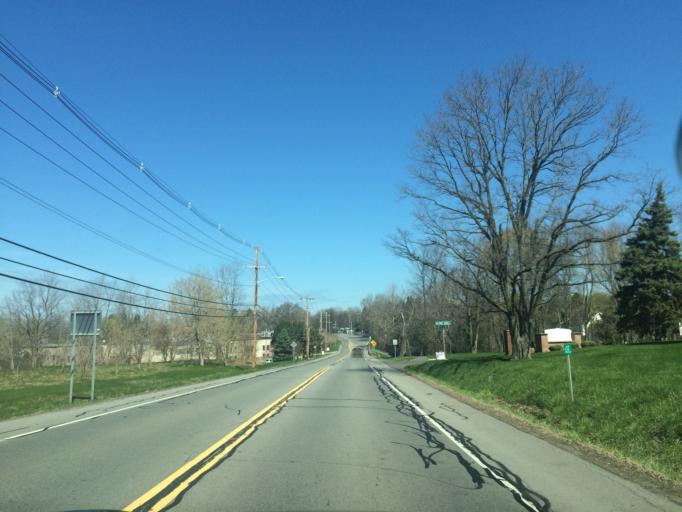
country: US
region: New York
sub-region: Monroe County
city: Fairport
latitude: 43.0998
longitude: -77.4293
